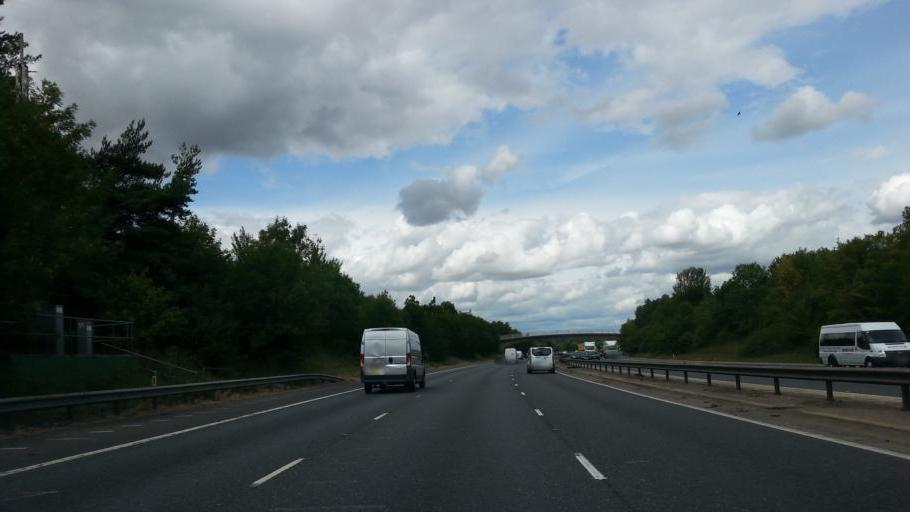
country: GB
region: England
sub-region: Essex
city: Little Hallingbury
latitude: 51.8502
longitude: 0.1847
